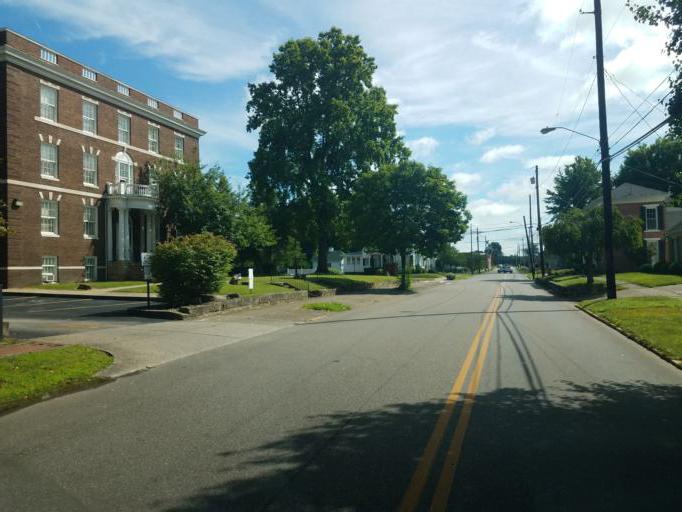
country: US
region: Ohio
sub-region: Gallia County
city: Gallipolis
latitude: 38.8093
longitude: -82.2010
